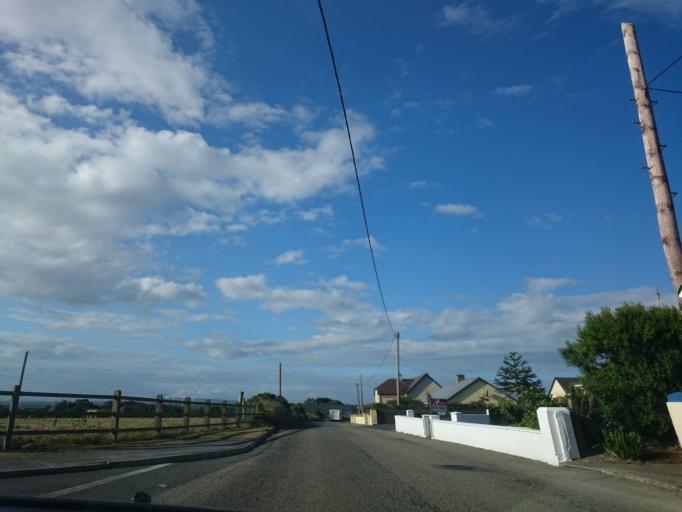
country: IE
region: Leinster
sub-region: Loch Garman
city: Loch Garman
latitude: 52.1787
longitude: -6.5839
